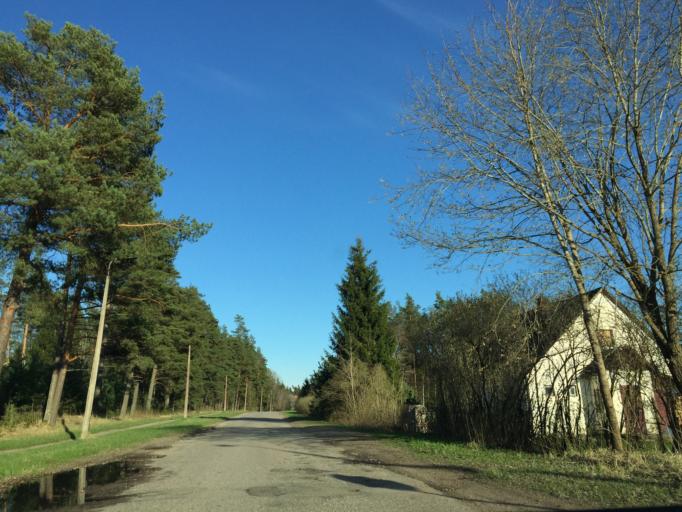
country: LV
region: Valkas Rajons
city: Valka
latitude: 57.7892
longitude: 25.9884
